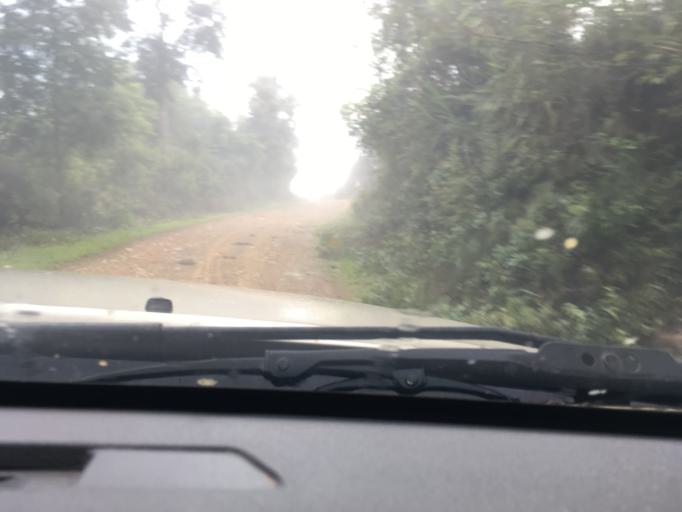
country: LA
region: Phongsali
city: Phongsali
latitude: 21.4283
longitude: 102.2623
